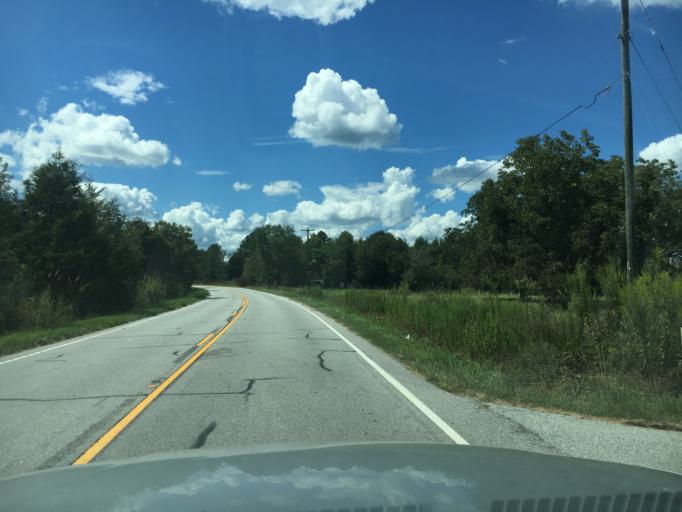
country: US
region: South Carolina
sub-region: Greenwood County
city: Ware Shoals
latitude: 34.5237
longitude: -82.1784
